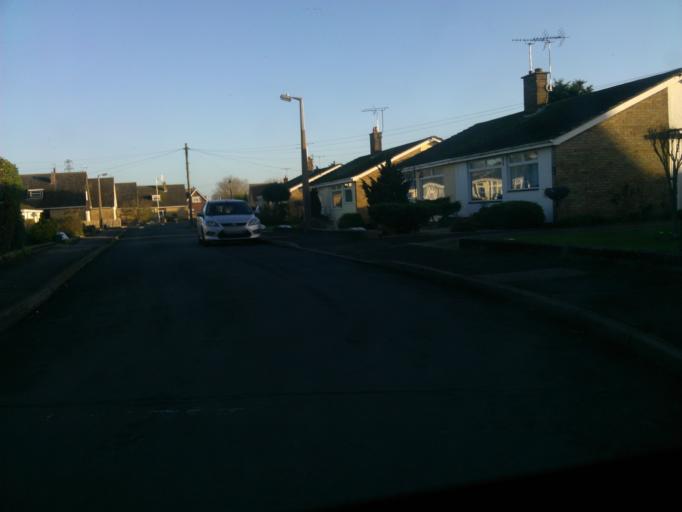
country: GB
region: England
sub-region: Essex
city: Wivenhoe
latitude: 51.8689
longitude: 0.9649
